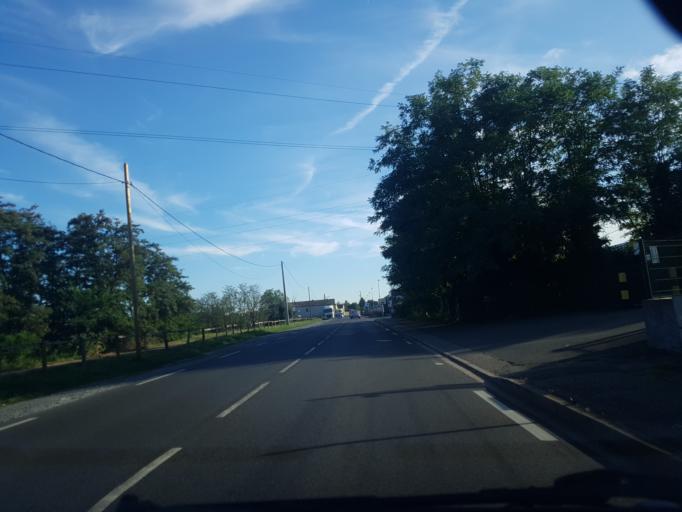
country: FR
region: Rhone-Alpes
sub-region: Departement du Rhone
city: Villefranche-sur-Saone
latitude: 45.9762
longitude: 4.7290
